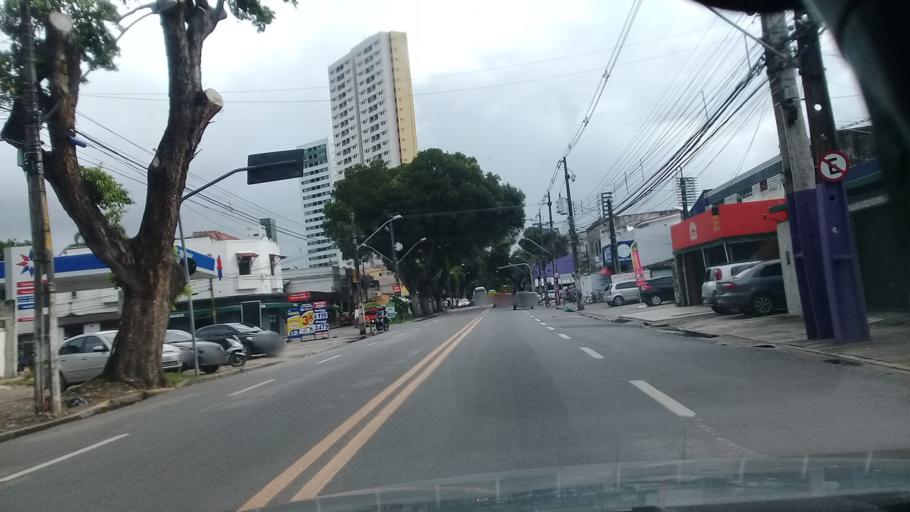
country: BR
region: Pernambuco
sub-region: Recife
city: Recife
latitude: -8.0332
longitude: -34.8848
